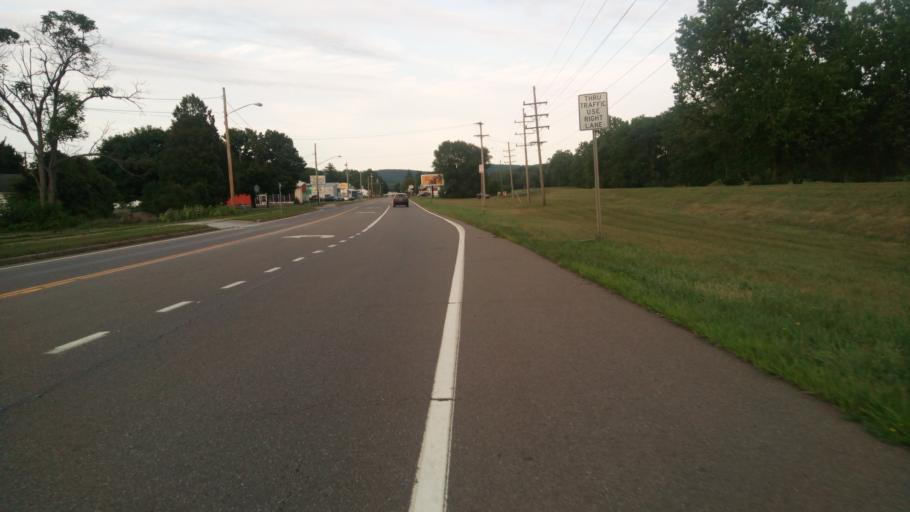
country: US
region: New York
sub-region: Chemung County
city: Southport
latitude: 42.0576
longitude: -76.8034
